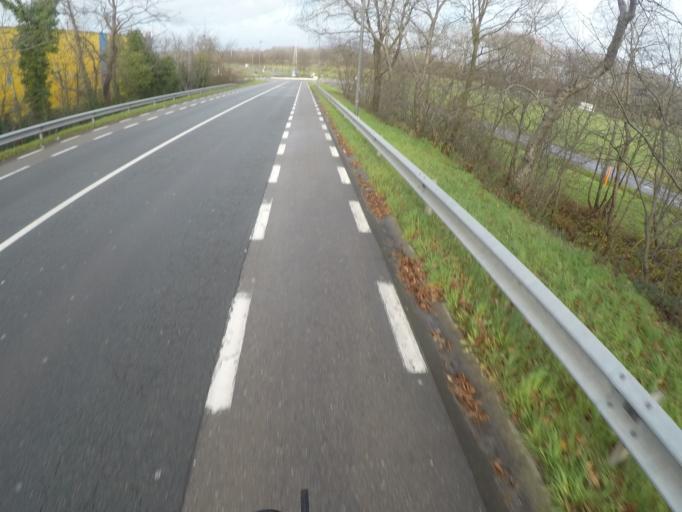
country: BE
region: Flanders
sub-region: Provincie Antwerpen
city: Wommelgem
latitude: 51.2133
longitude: 4.5276
